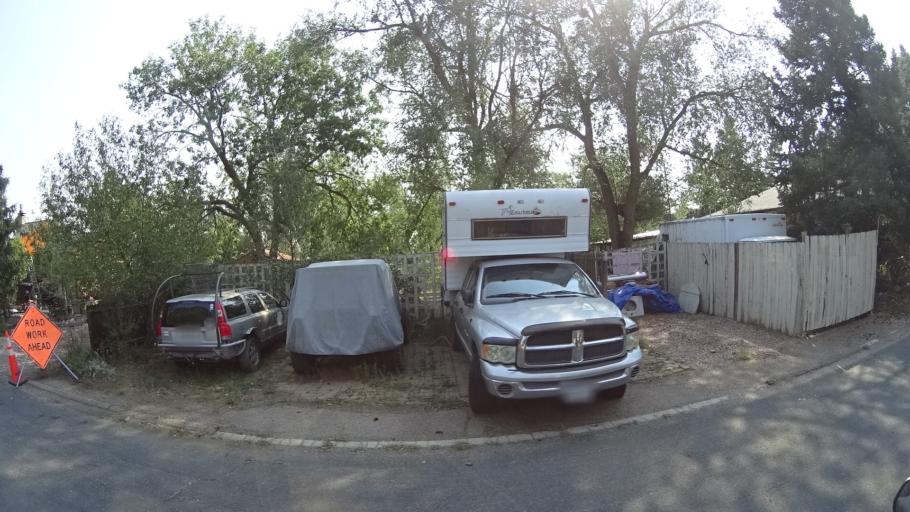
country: US
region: Colorado
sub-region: El Paso County
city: Colorado Springs
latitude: 38.8132
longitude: -104.8344
